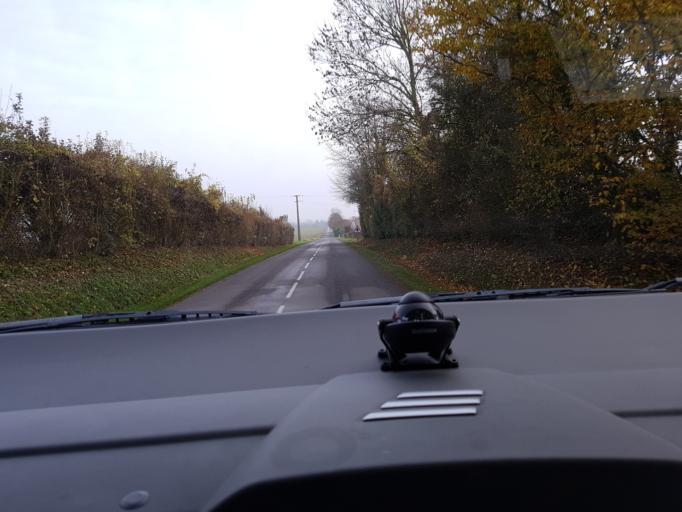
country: FR
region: Lower Normandy
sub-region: Departement de l'Orne
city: Mortree
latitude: 48.6362
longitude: 0.0487
